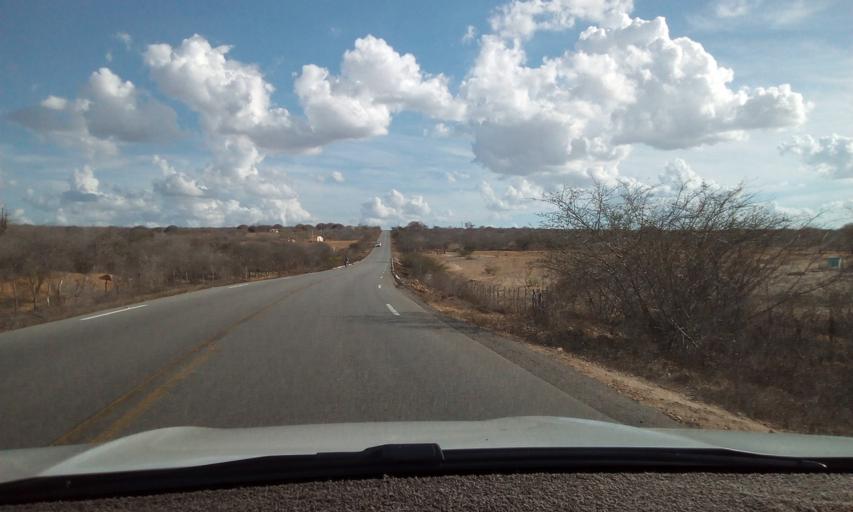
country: BR
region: Paraiba
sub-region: Soledade
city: Soledade
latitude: -6.8763
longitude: -36.3995
